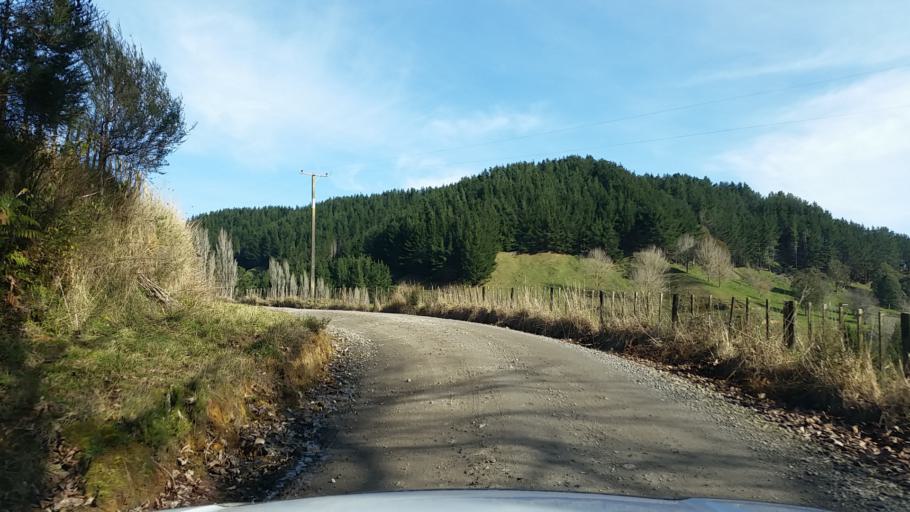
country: NZ
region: Taranaki
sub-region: South Taranaki District
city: Eltham
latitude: -39.3551
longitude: 174.5135
